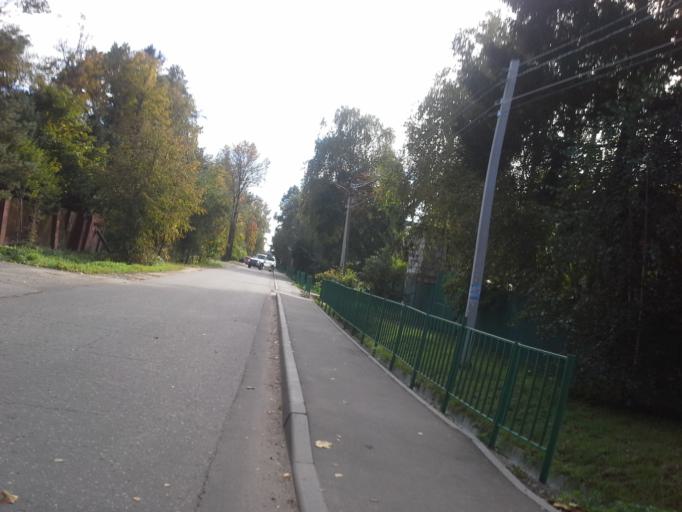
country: RU
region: Moskovskaya
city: Zhavoronki
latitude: 55.6471
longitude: 37.0978
